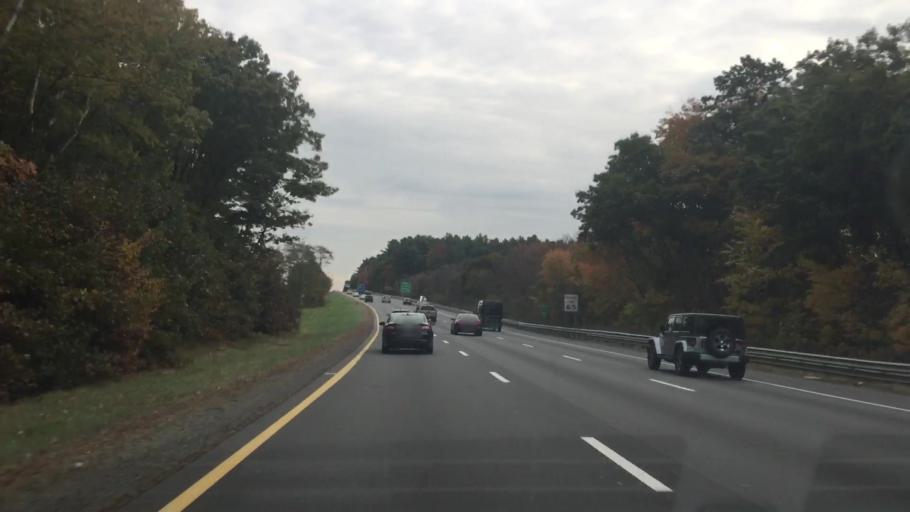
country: US
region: Massachusetts
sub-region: Middlesex County
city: Tewksbury
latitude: 42.6499
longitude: -71.2142
